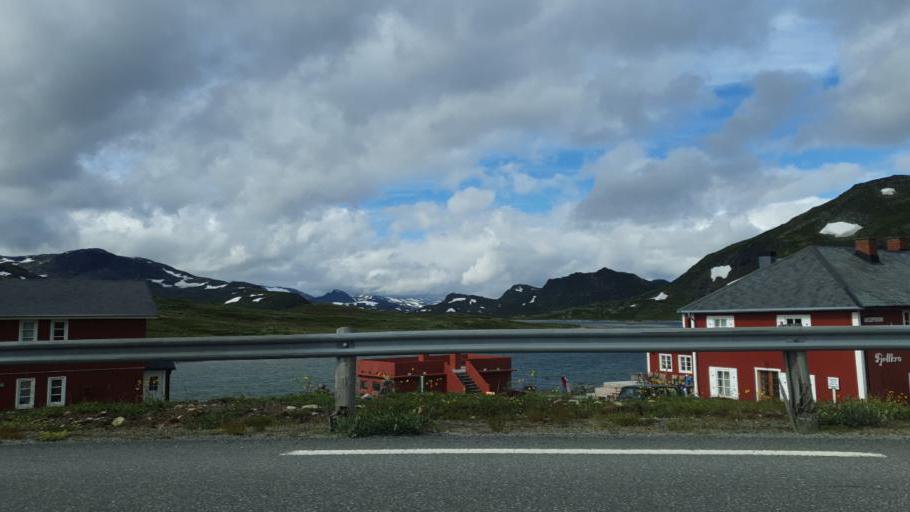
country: NO
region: Oppland
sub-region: Vestre Slidre
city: Slidre
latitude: 61.3276
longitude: 8.7998
